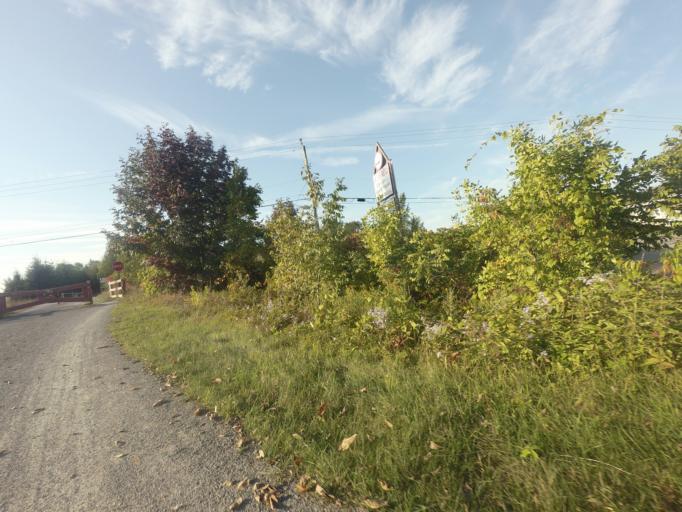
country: CA
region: Quebec
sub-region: Laurentides
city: Saint-Jerome
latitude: 45.8088
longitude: -74.0187
